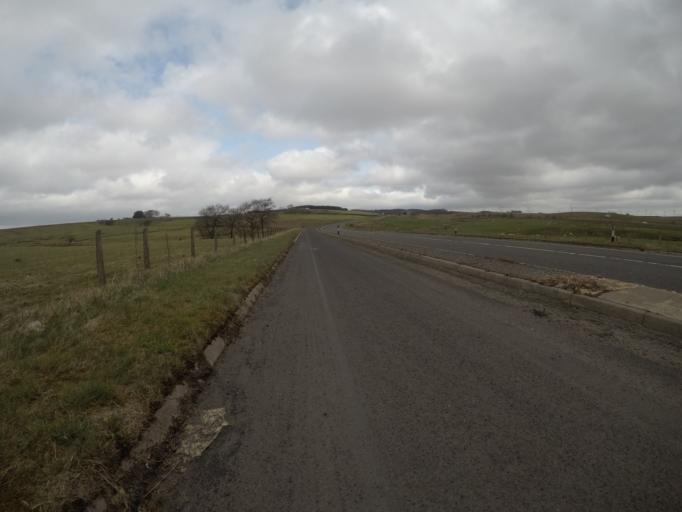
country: GB
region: Scotland
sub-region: East Ayrshire
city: Galston
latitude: 55.6890
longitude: -4.4110
